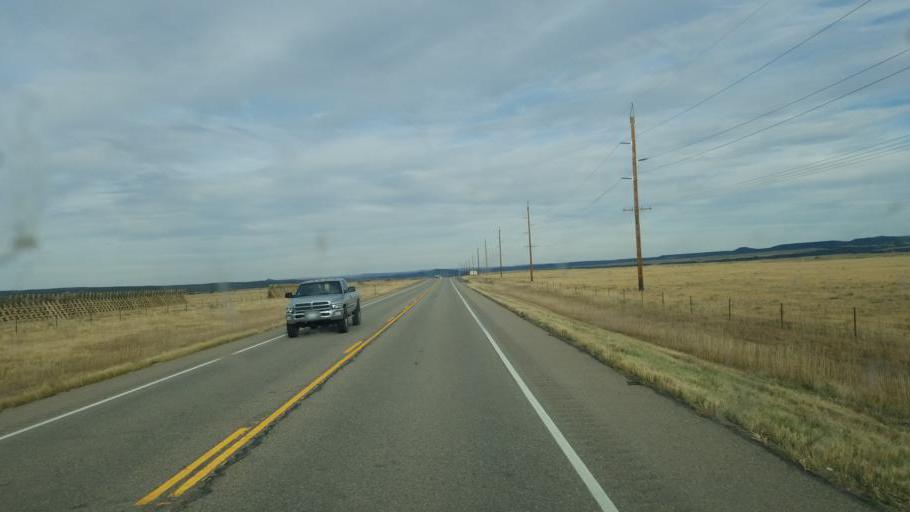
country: US
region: Colorado
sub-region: Huerfano County
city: Walsenburg
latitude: 37.5459
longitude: -104.9984
